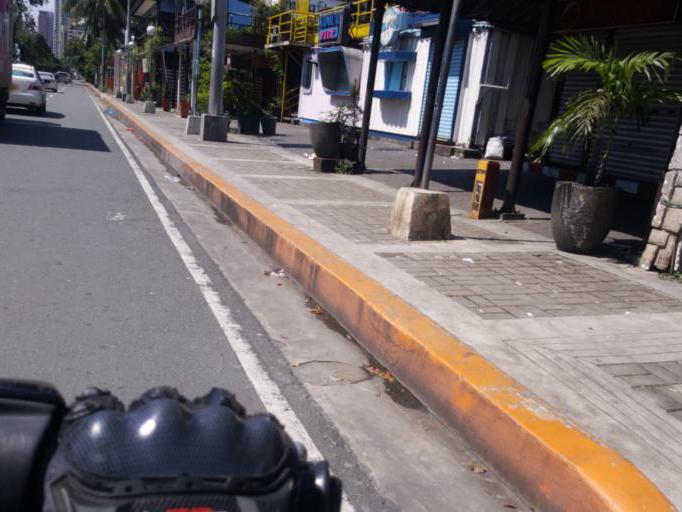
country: PH
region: Metro Manila
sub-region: City of Manila
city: Port Area
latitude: 14.5694
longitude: 120.9831
